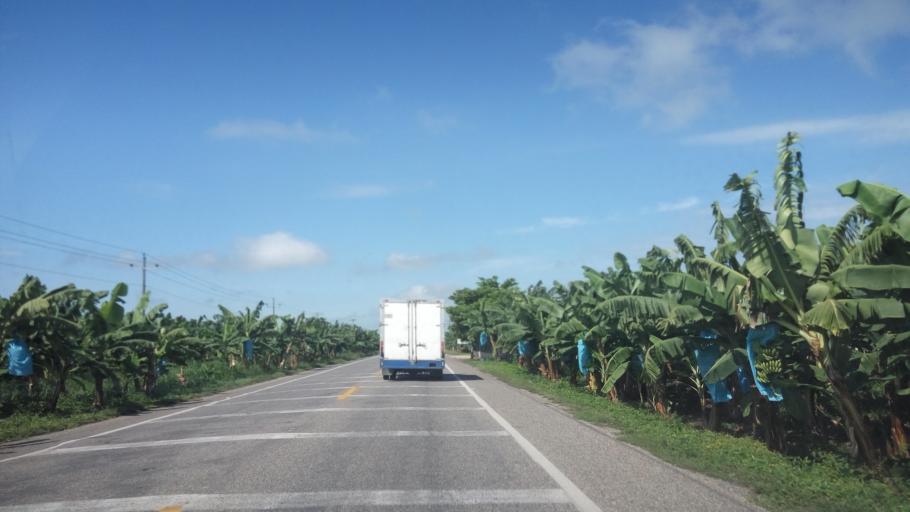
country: MX
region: Tabasco
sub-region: Teapa
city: Eureka y Belen
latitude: 17.6538
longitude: -92.9581
